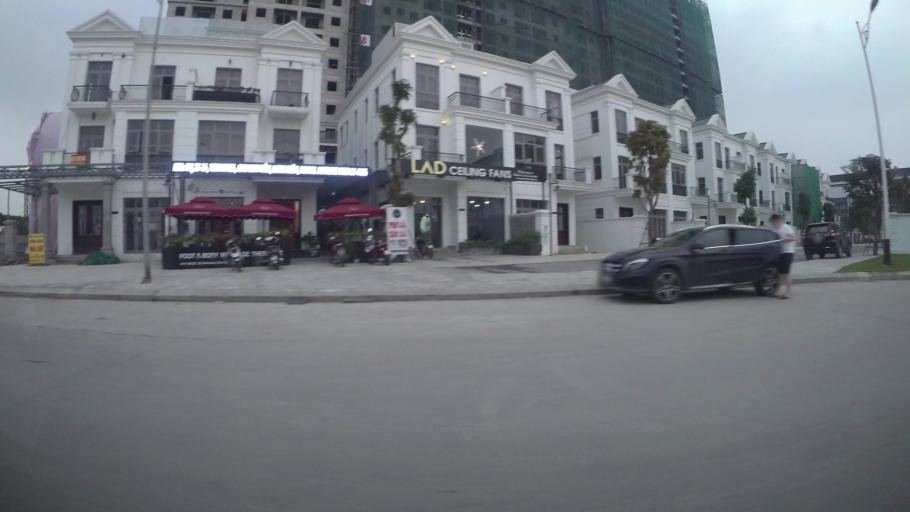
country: VN
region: Ha Noi
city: Trau Quy
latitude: 21.0427
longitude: 105.9056
